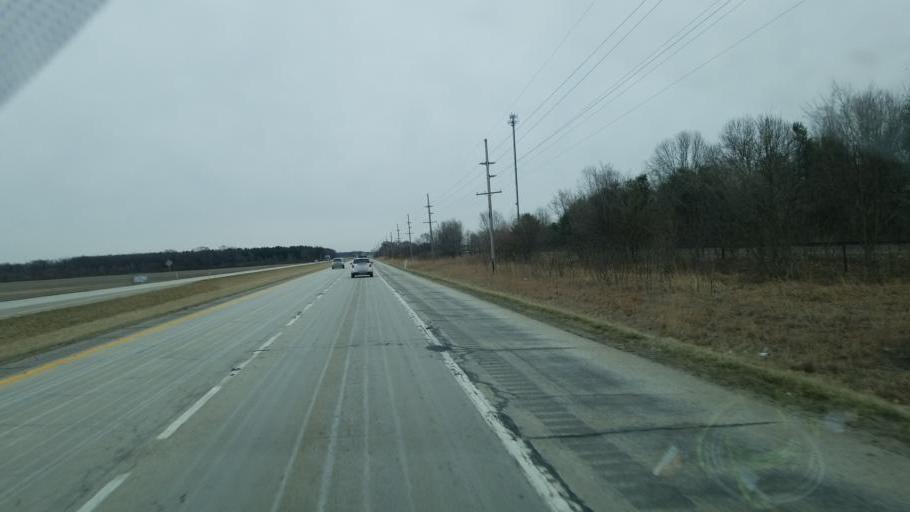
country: US
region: Indiana
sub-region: Starke County
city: Koontz Lake
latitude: 41.3781
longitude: -86.5522
